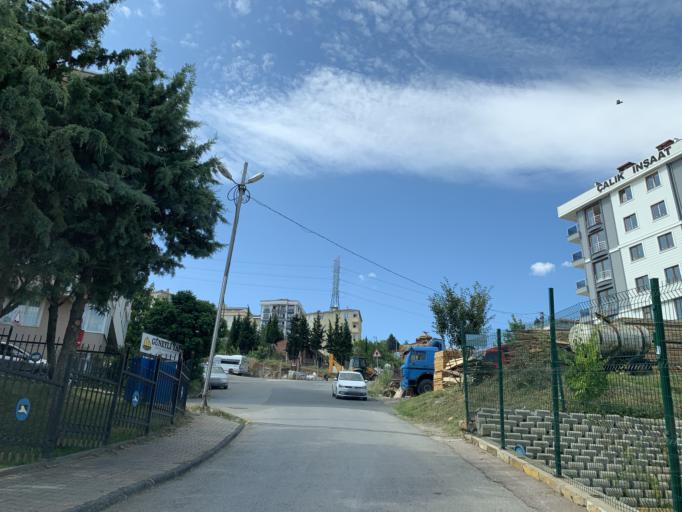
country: TR
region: Istanbul
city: Pendik
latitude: 40.8943
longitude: 29.2433
